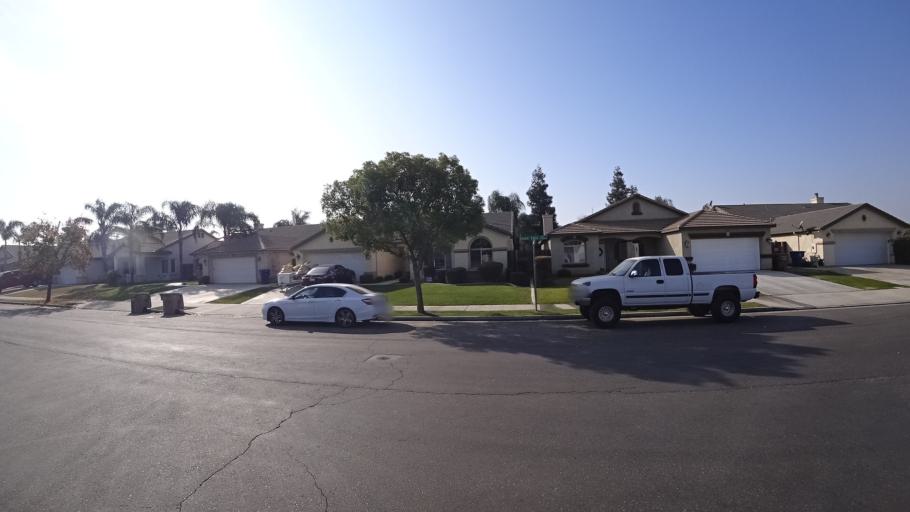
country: US
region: California
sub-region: Kern County
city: Greenacres
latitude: 35.4141
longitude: -119.1158
